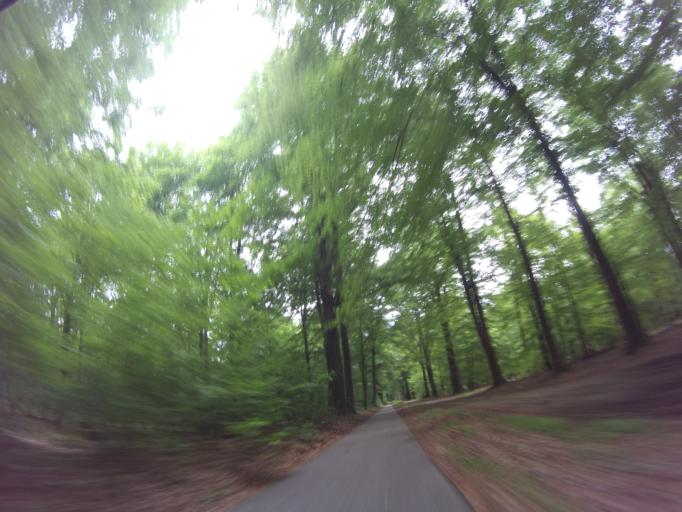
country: NL
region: Drenthe
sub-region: Gemeente Emmen
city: Emmen
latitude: 52.8251
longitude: 6.8808
